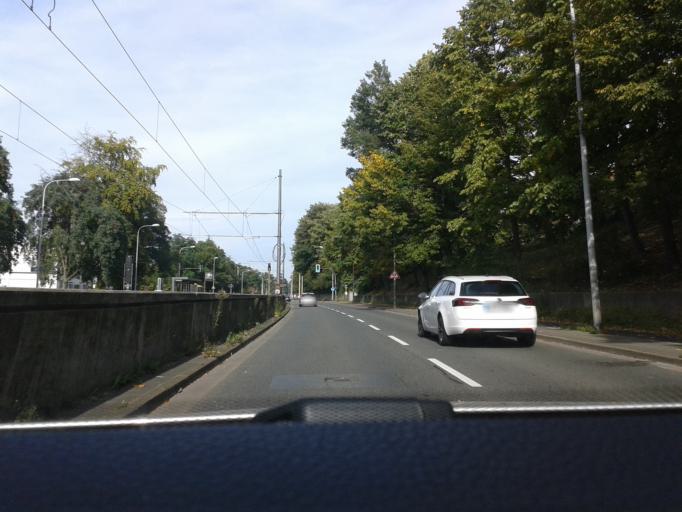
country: DE
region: North Rhine-Westphalia
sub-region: Regierungsbezirk Dusseldorf
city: Muelheim (Ruhr)
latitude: 51.4411
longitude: 6.8874
